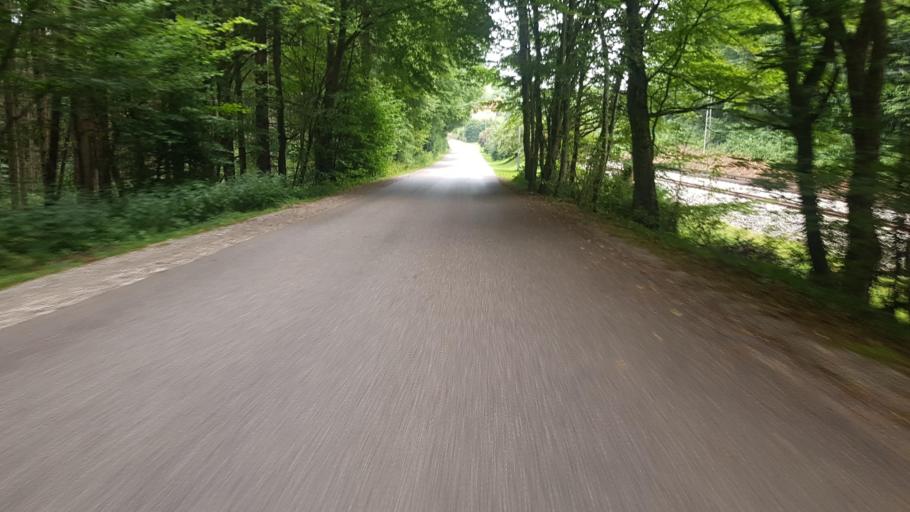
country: DE
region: Bavaria
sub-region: Upper Bavaria
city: Starnberg
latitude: 48.0276
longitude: 11.3501
